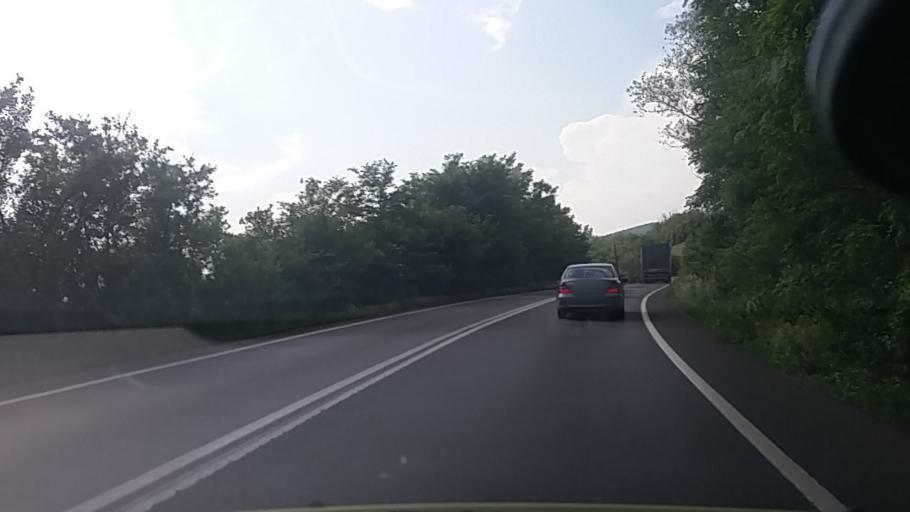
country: RO
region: Arad
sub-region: Comuna Varadia de Mures
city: Varadia de Mures
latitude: 46.0312
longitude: 22.1061
